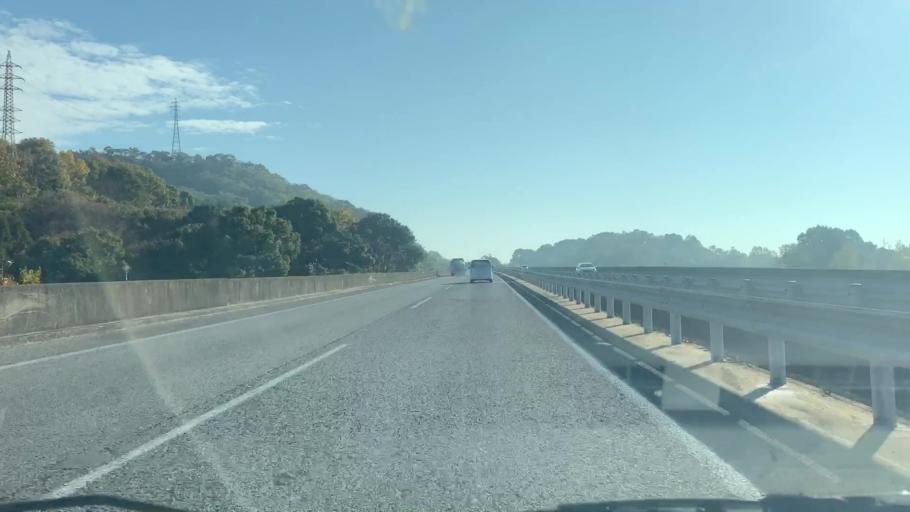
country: JP
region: Saga Prefecture
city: Saga-shi
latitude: 33.2874
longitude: 130.1476
